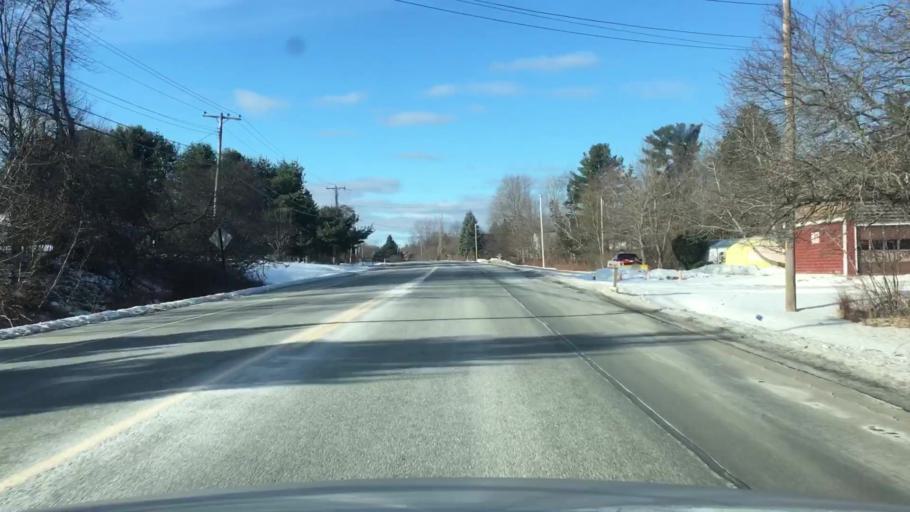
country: US
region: Maine
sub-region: Penobscot County
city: Eddington
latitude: 44.8200
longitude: -68.6482
